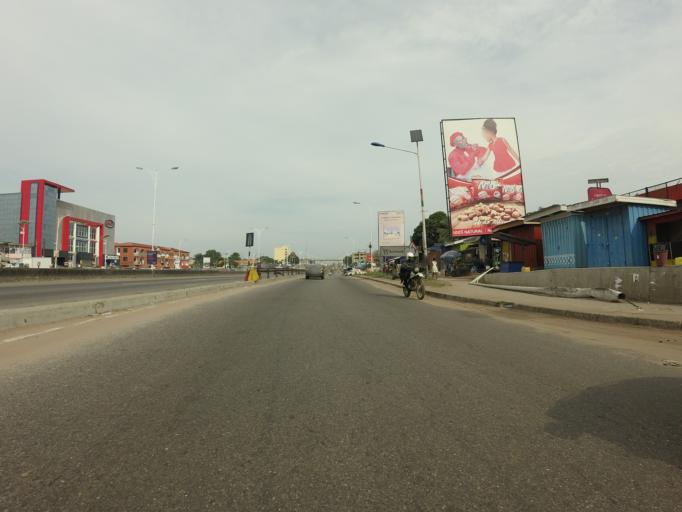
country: GH
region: Greater Accra
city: Dome
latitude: 5.6249
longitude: -0.2334
